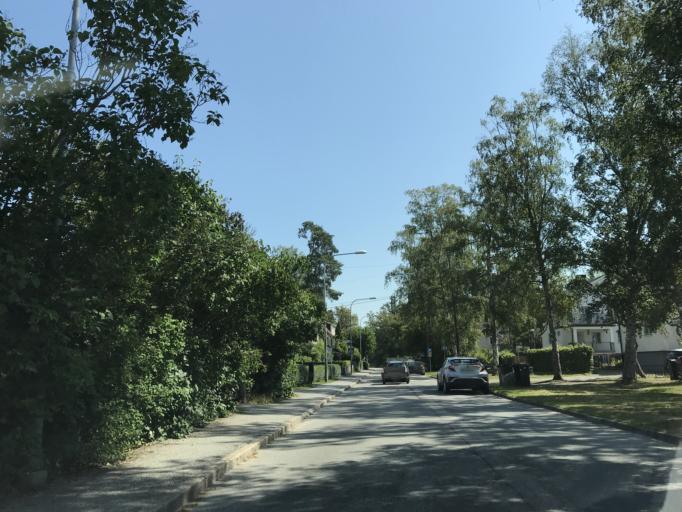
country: SE
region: Stockholm
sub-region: Stockholms Kommun
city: Bromma
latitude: 59.3250
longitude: 17.9659
